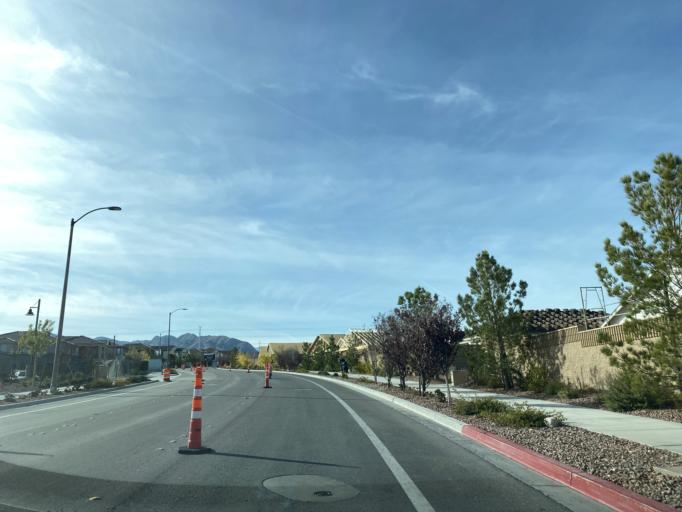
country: US
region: Nevada
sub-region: Clark County
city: Summerlin South
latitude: 36.3106
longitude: -115.3248
